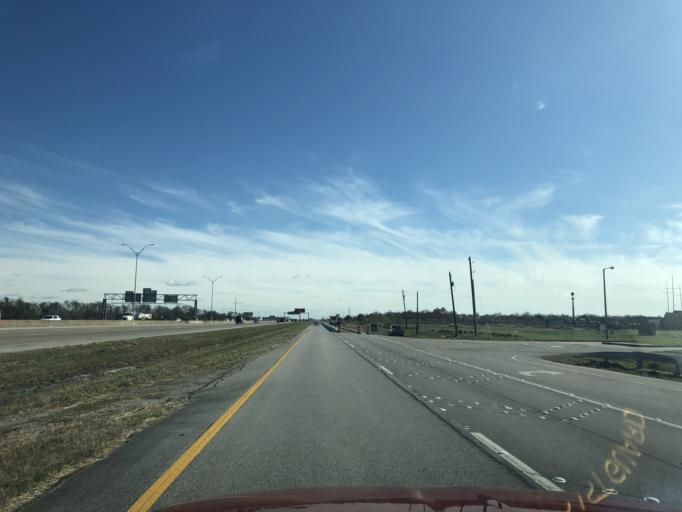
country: US
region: Texas
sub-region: Galveston County
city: Dickinson
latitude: 29.4256
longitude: -95.0559
